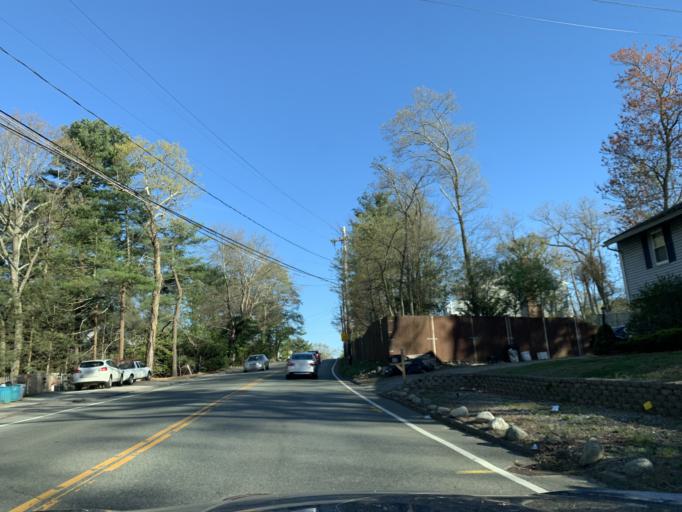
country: US
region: Massachusetts
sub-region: Norfolk County
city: Canton
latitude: 42.1368
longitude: -71.1464
